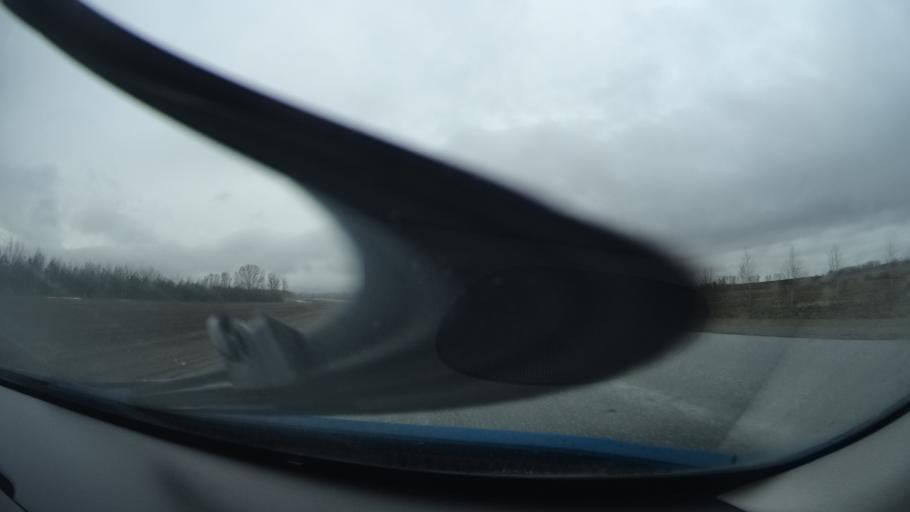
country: RU
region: Bashkortostan
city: Kandry
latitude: 54.5138
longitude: 53.9677
